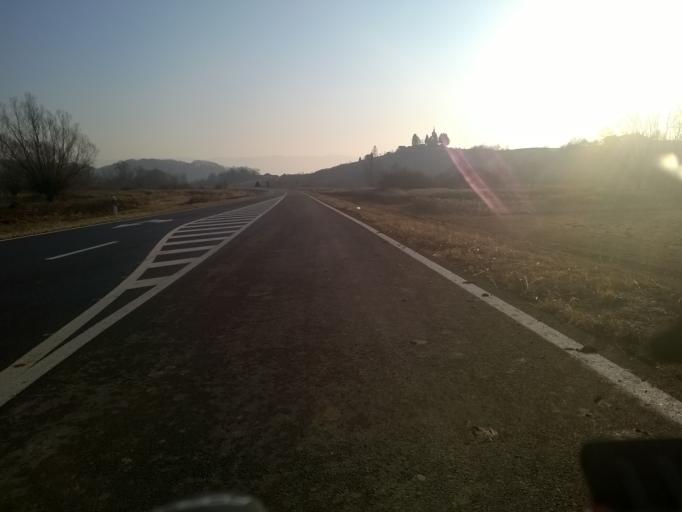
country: HR
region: Krapinsko-Zagorska
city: Zabok
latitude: 46.0447
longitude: 15.9143
